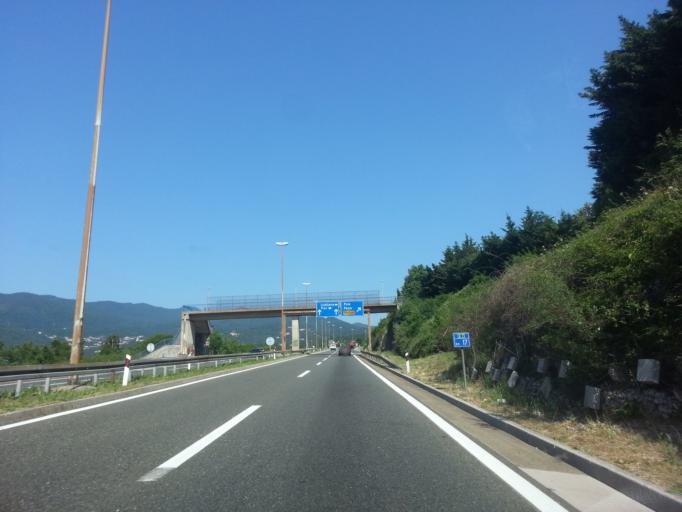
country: HR
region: Primorsko-Goranska
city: Rubesi
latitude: 45.3591
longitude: 14.3416
